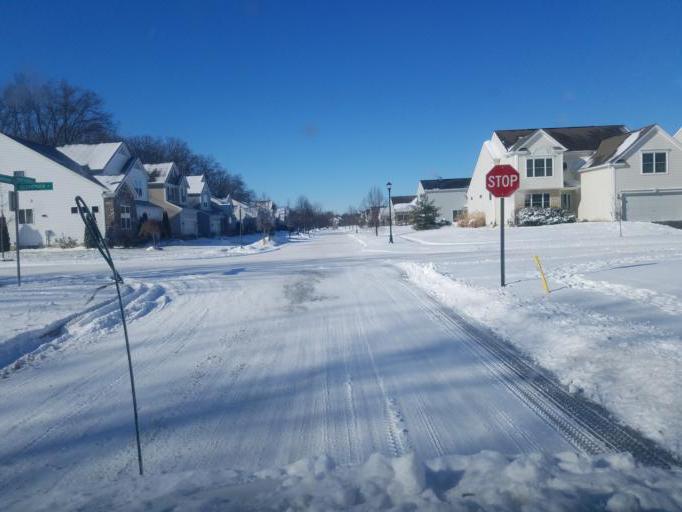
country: US
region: Ohio
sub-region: Franklin County
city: Worthington
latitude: 40.1437
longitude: -83.0085
